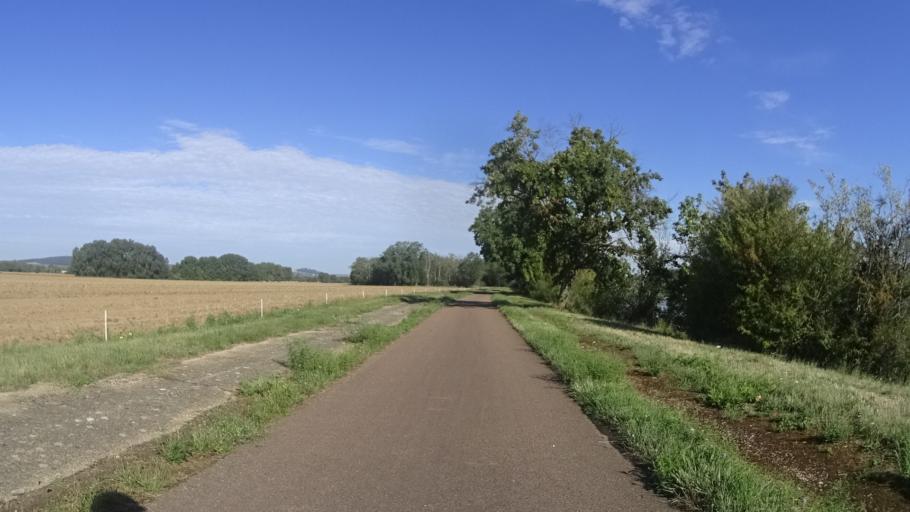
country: FR
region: Bourgogne
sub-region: Departement de la Nievre
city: Pouilly-sur-Loire
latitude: 47.2939
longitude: 2.9262
